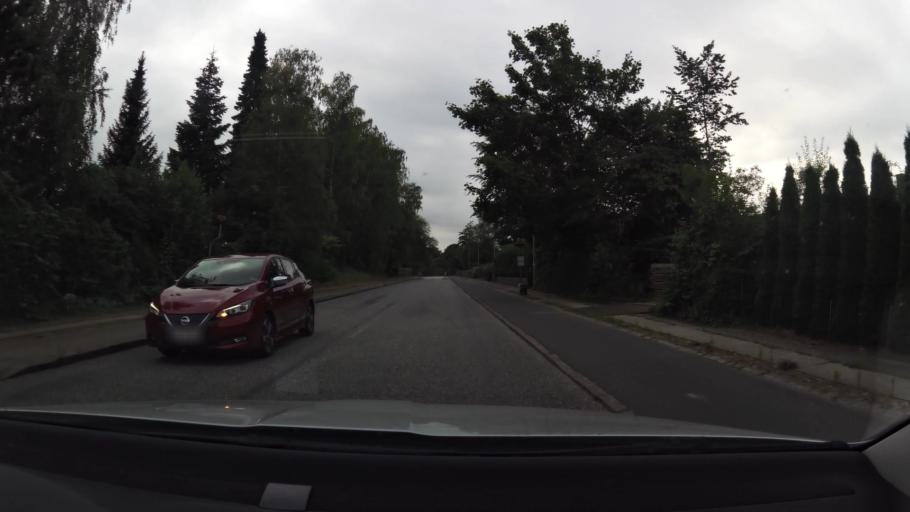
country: DK
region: Capital Region
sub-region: Lyngby-Tarbaek Kommune
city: Kongens Lyngby
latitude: 55.7987
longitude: 12.5105
